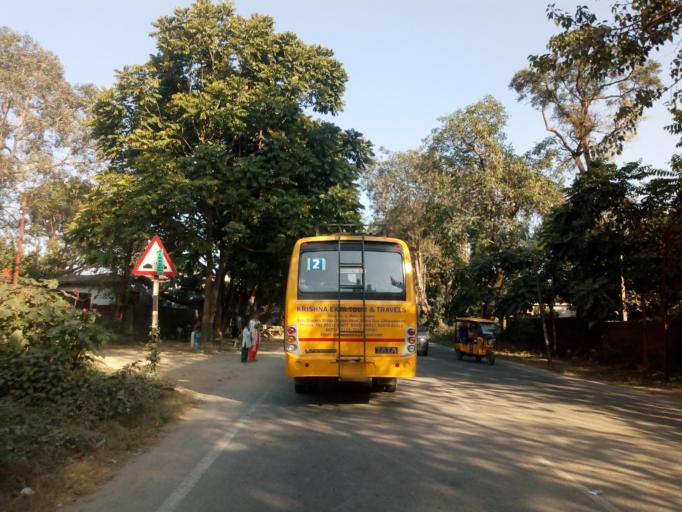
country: IN
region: Uttarakhand
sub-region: Dehradun
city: Dehradun
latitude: 30.3490
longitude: 77.8887
